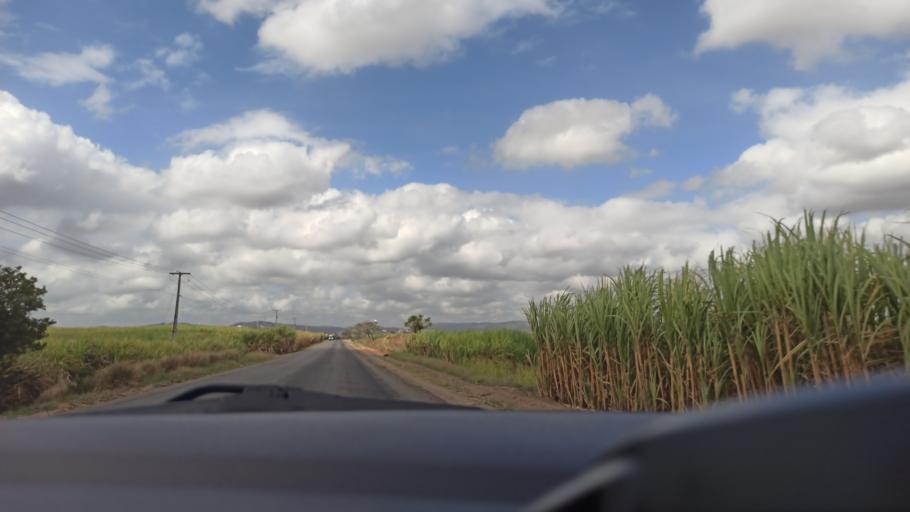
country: BR
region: Pernambuco
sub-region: Timbauba
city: Timbauba
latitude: -7.4858
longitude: -35.2920
